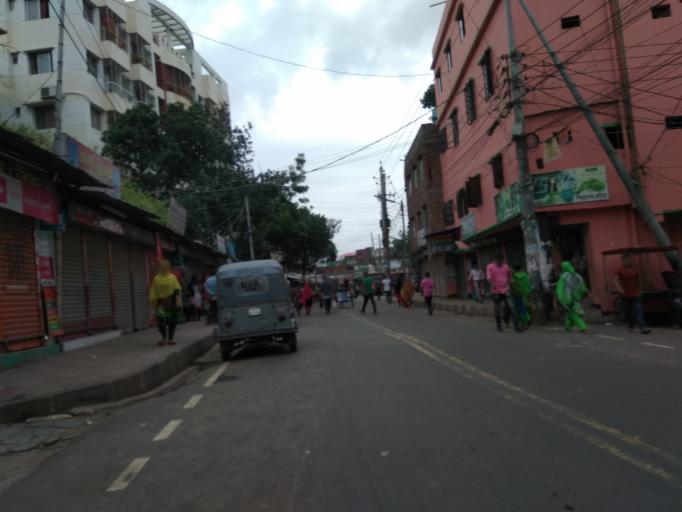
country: BD
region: Dhaka
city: Tungi
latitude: 23.8176
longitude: 90.3615
